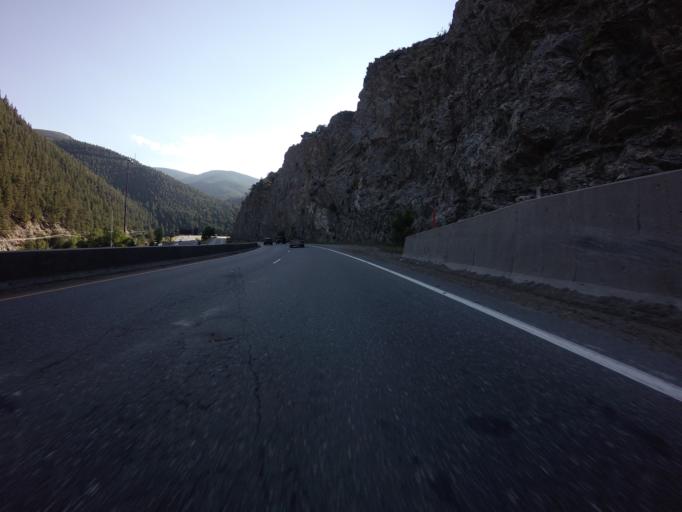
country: US
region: Colorado
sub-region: Clear Creek County
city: Idaho Springs
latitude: 39.7458
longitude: -105.4393
